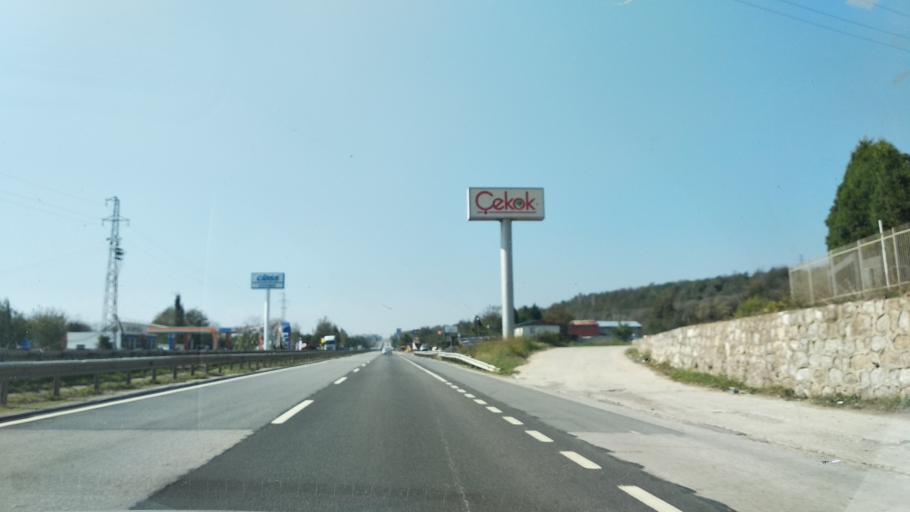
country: TR
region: Kocaeli
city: Derbent
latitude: 40.7324
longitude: 30.1937
